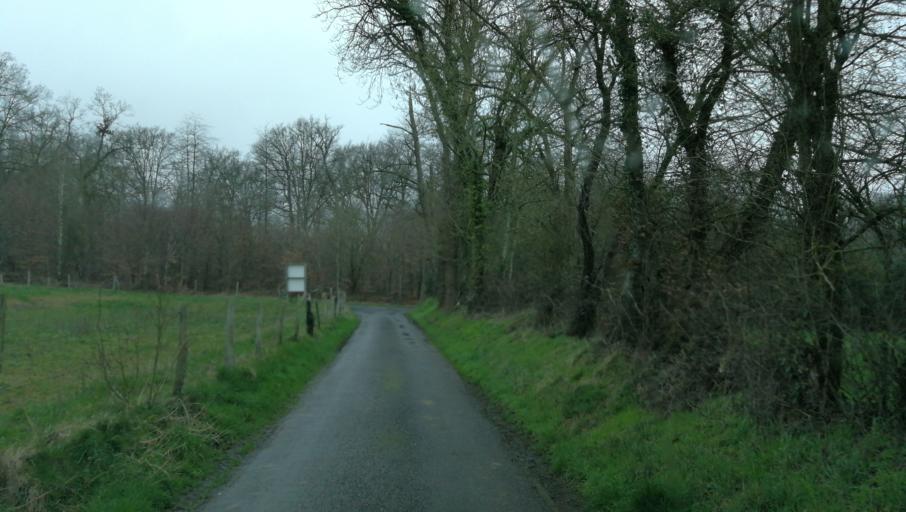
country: FR
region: Haute-Normandie
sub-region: Departement de l'Eure
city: Brionne
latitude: 49.1796
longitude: 0.6965
